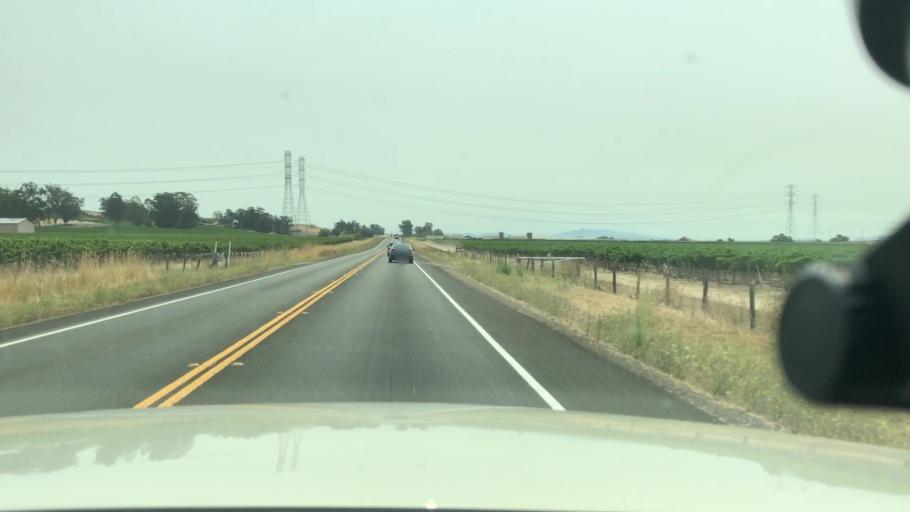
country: US
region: California
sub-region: Marin County
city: Black Point-Green Point
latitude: 38.1648
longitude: -122.5097
